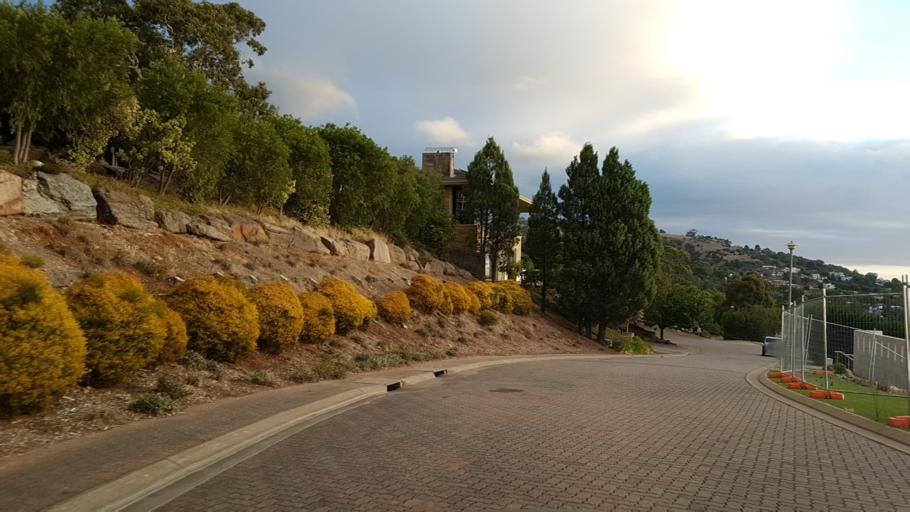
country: AU
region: South Australia
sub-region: Burnside
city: Beaumont
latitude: -34.9451
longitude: 138.6698
